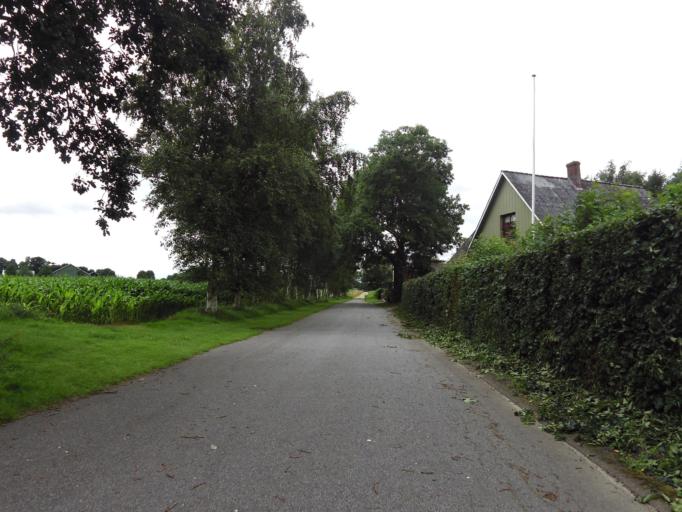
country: DK
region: South Denmark
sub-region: Haderslev Kommune
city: Gram
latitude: 55.2755
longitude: 9.1702
